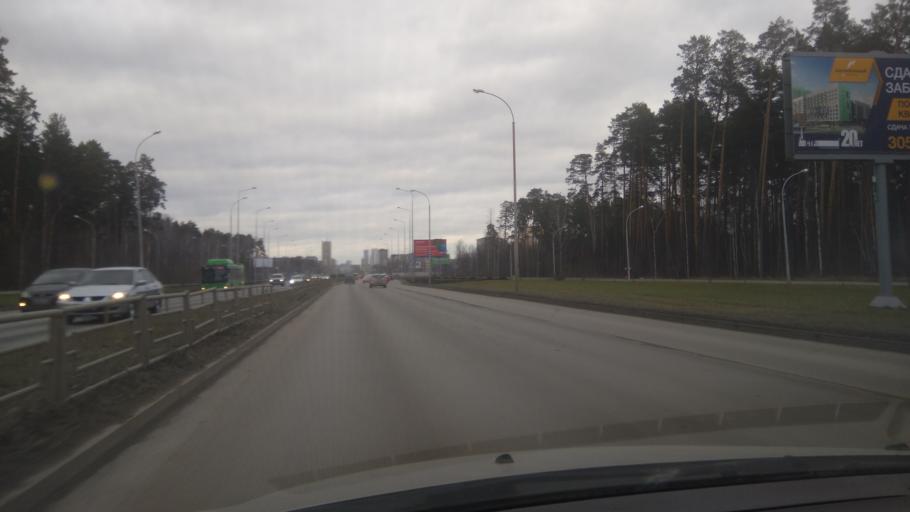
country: RU
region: Sverdlovsk
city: Sovkhoznyy
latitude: 56.8003
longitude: 60.5344
